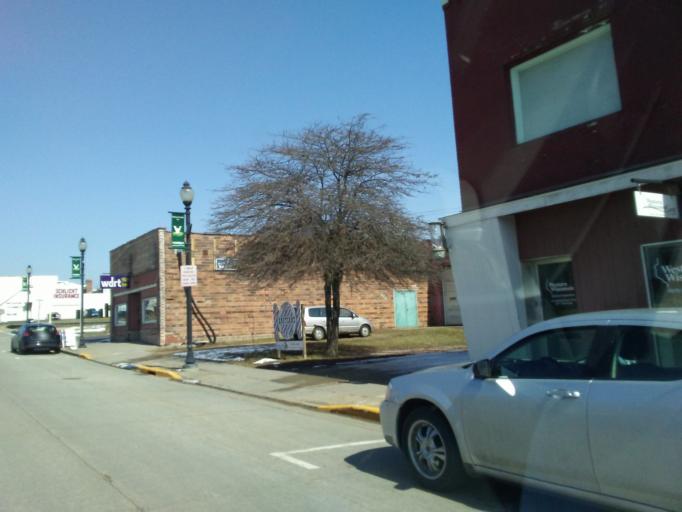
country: US
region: Wisconsin
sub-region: Vernon County
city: Viroqua
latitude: 43.5532
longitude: -90.8892
